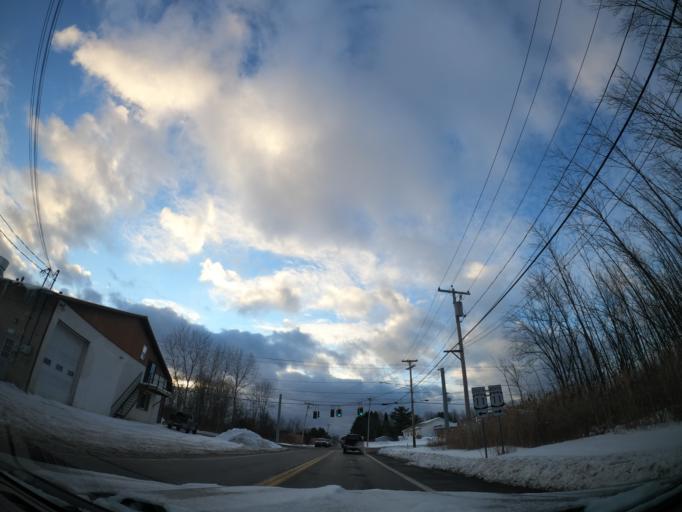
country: US
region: New York
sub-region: Onondaga County
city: Brewerton
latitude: 43.2171
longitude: -76.1340
